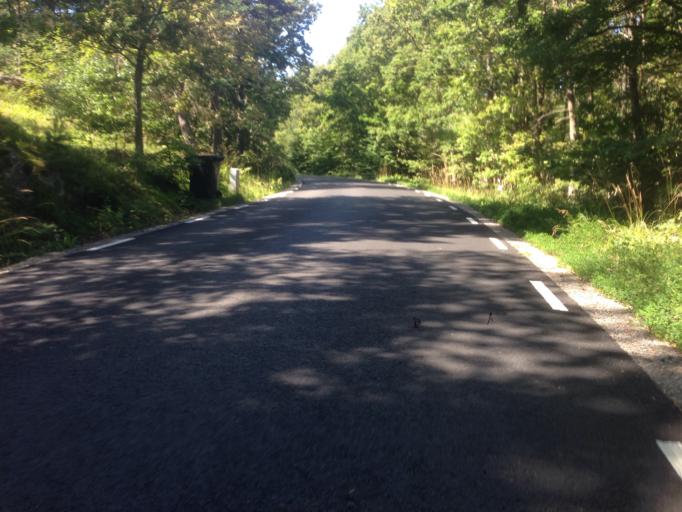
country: SE
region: Stockholm
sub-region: Vaxholms Kommun
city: Vaxholm
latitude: 59.3830
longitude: 18.3706
